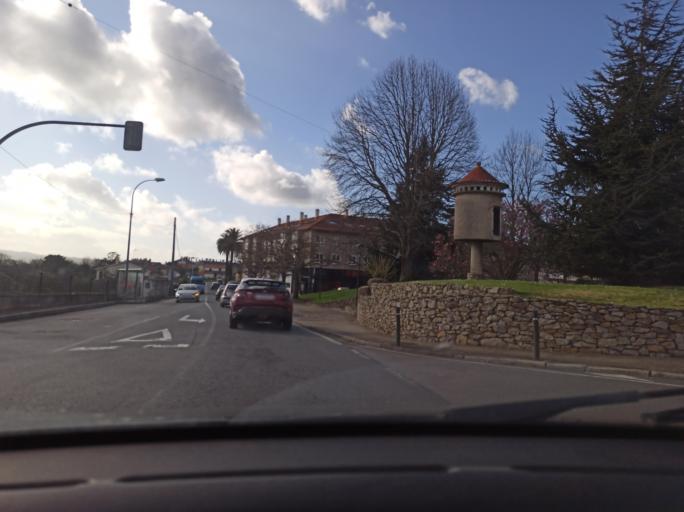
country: ES
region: Galicia
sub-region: Provincia da Coruna
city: Oleiros
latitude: 43.3327
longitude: -8.3173
